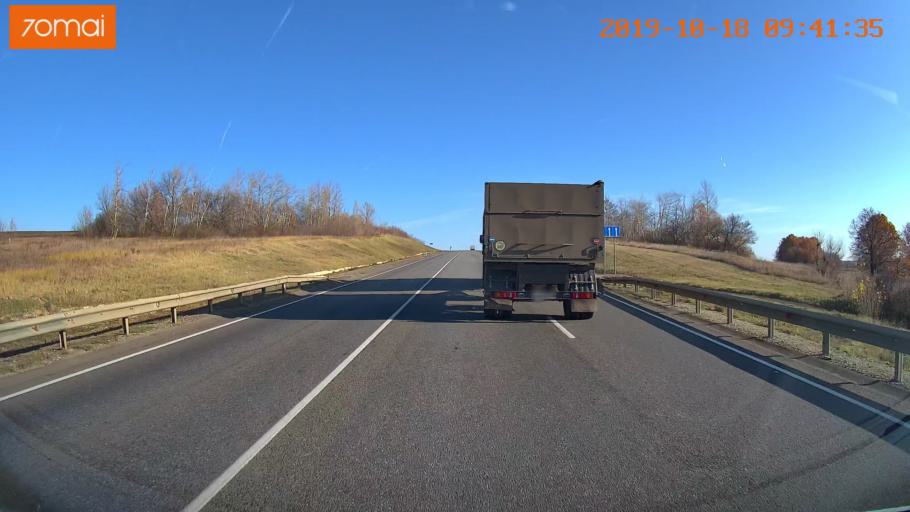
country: RU
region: Tula
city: Kazachka
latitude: 53.2765
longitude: 38.1638
